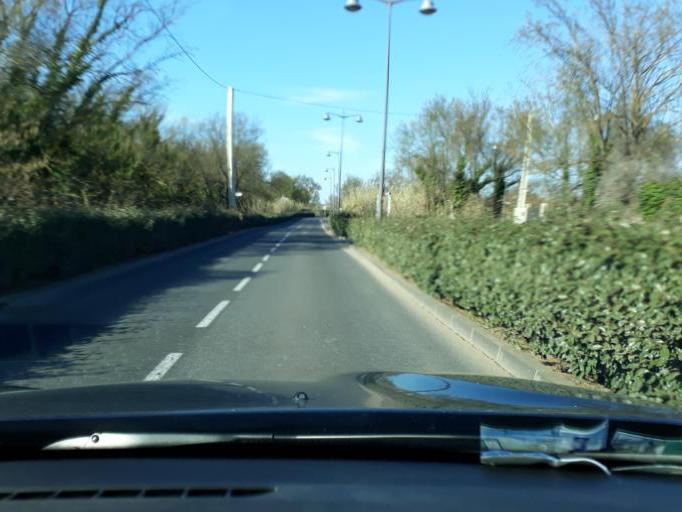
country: FR
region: Languedoc-Roussillon
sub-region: Departement de l'Herault
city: Agde
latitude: 43.3124
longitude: 3.4642
